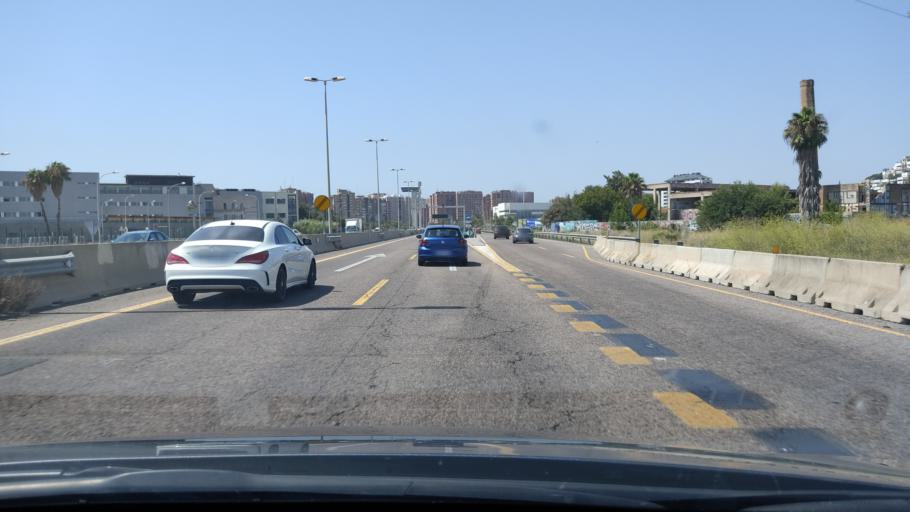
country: ES
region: Valencia
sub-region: Provincia de Valencia
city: Alboraya
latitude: 39.4846
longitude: -0.3466
